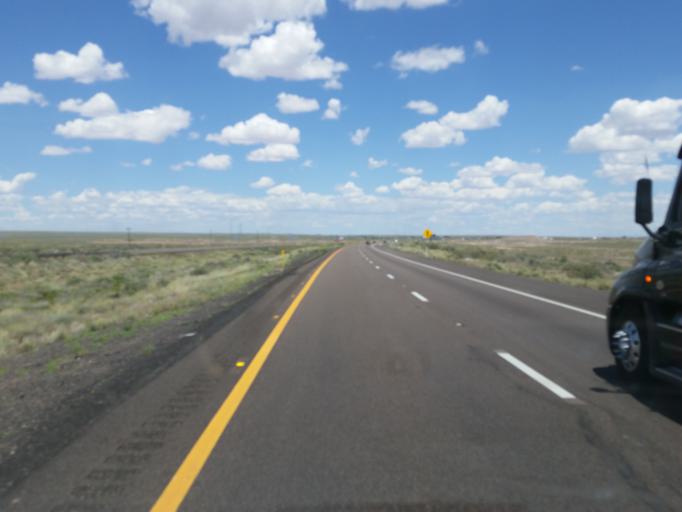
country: US
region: Arizona
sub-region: Navajo County
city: Holbrook
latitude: 34.9735
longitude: -110.0860
